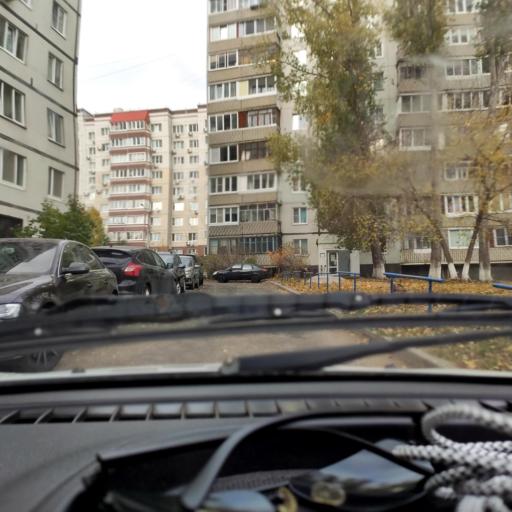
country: RU
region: Samara
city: Zhigulevsk
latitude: 53.4785
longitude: 49.4709
